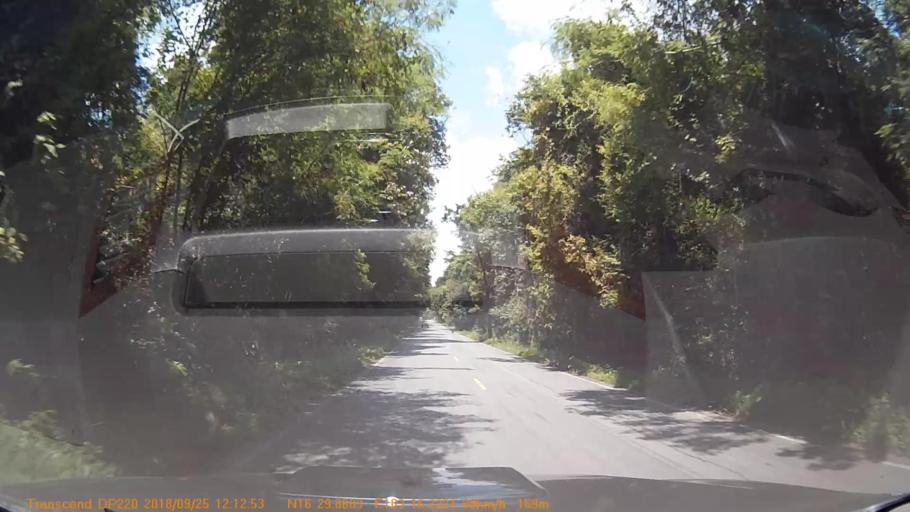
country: TH
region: Kalasin
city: Huai Mek
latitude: 16.4979
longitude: 103.2704
